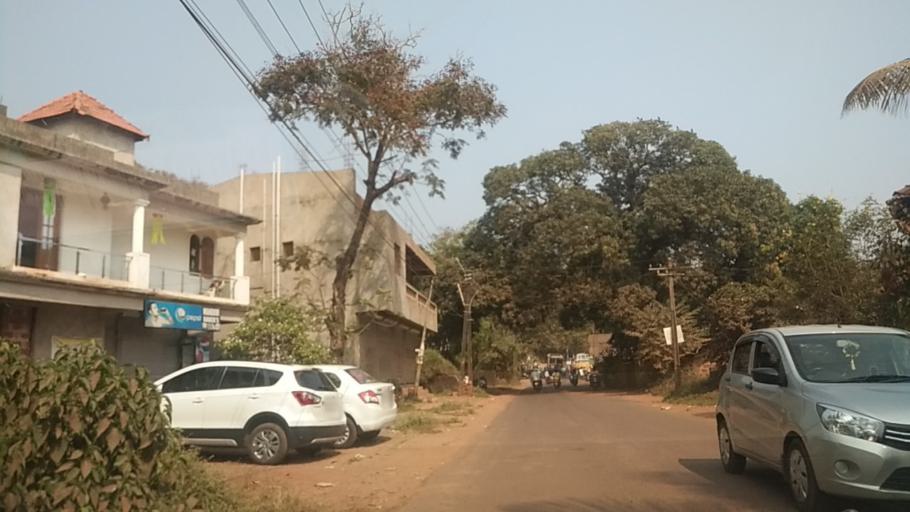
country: IN
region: Goa
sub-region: North Goa
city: Panaji
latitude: 15.5060
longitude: 73.8272
